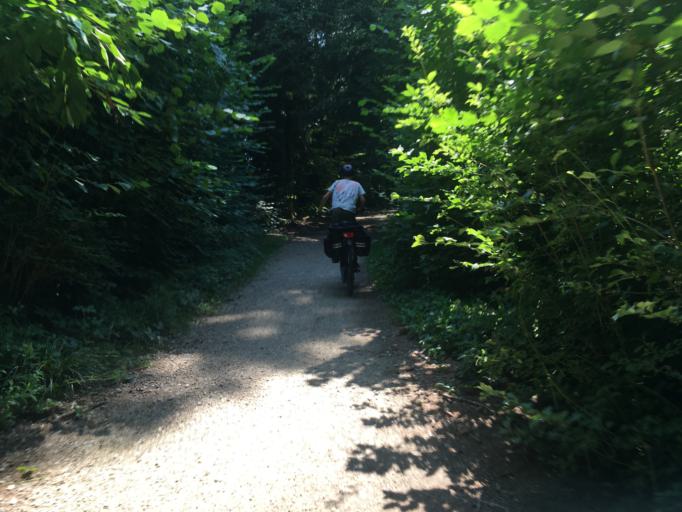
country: CH
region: Bern
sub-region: Emmental District
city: Lauperswil
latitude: 46.9467
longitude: 7.7497
